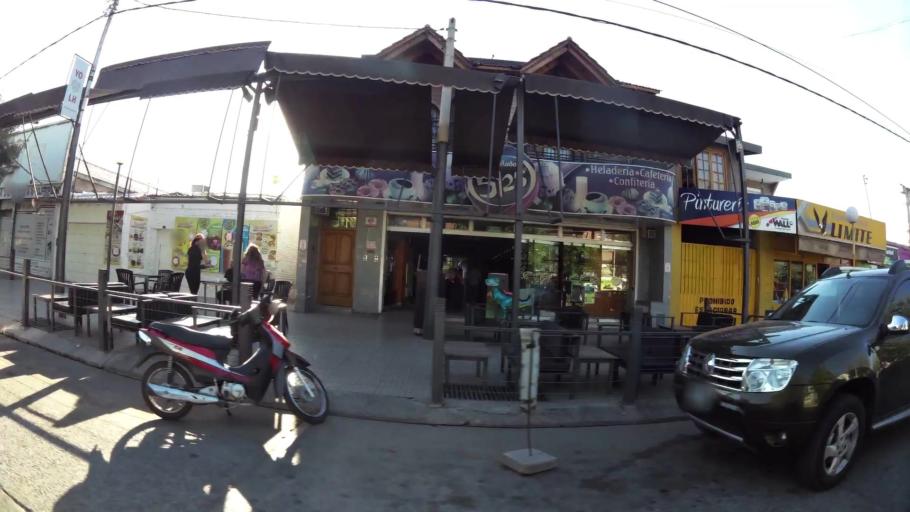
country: AR
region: Mendoza
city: Las Heras
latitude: -32.8662
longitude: -68.8225
